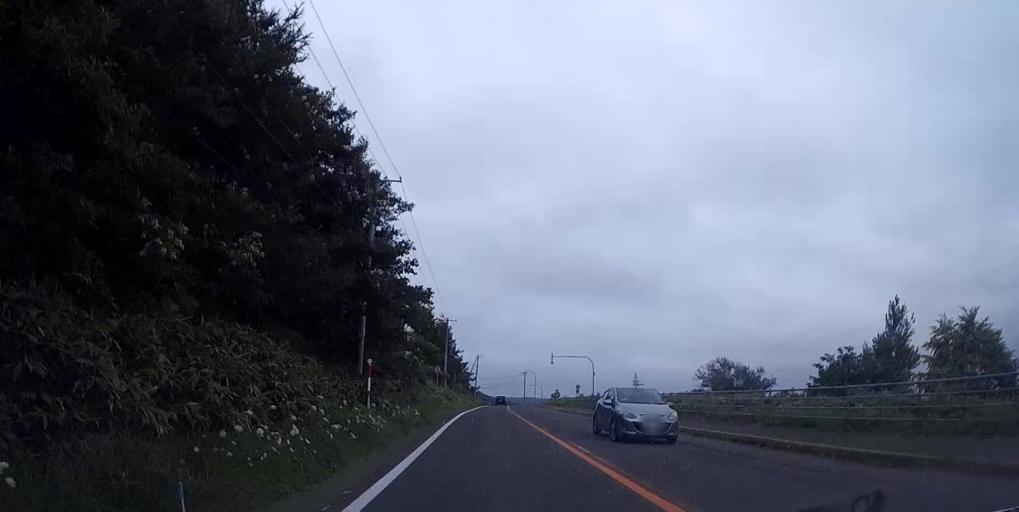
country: JP
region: Hokkaido
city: Iwanai
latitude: 42.4176
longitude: 139.8910
